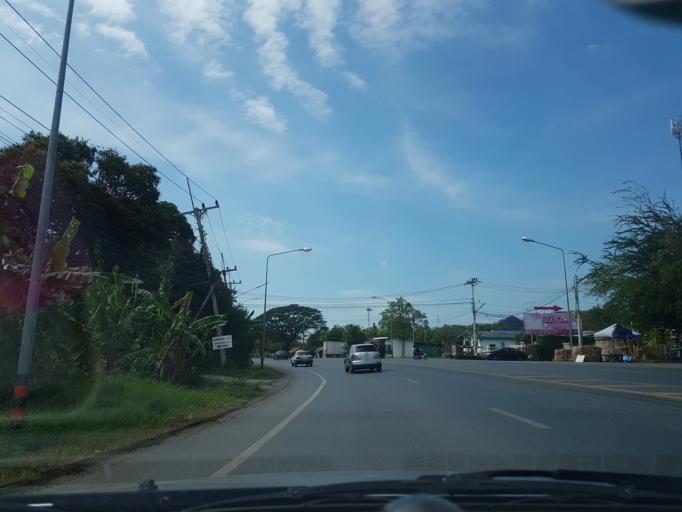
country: TH
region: Lop Buri
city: Lop Buri
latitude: 14.8007
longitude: 100.7211
